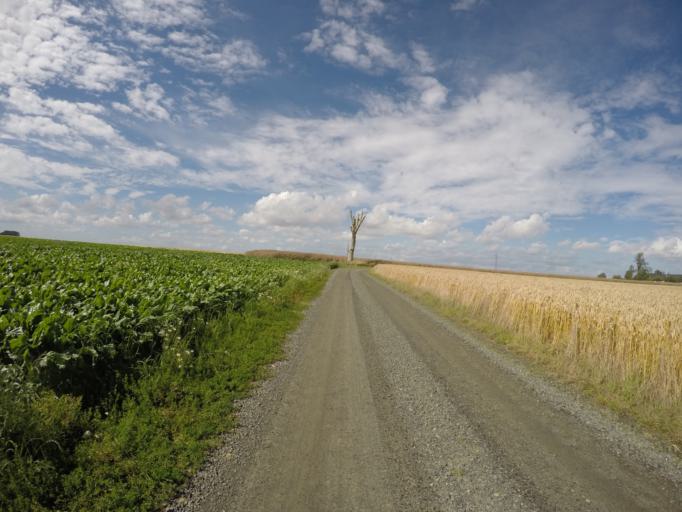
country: SE
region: Skane
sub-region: Tomelilla Kommun
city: Tomelilla
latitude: 55.4660
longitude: 14.1366
